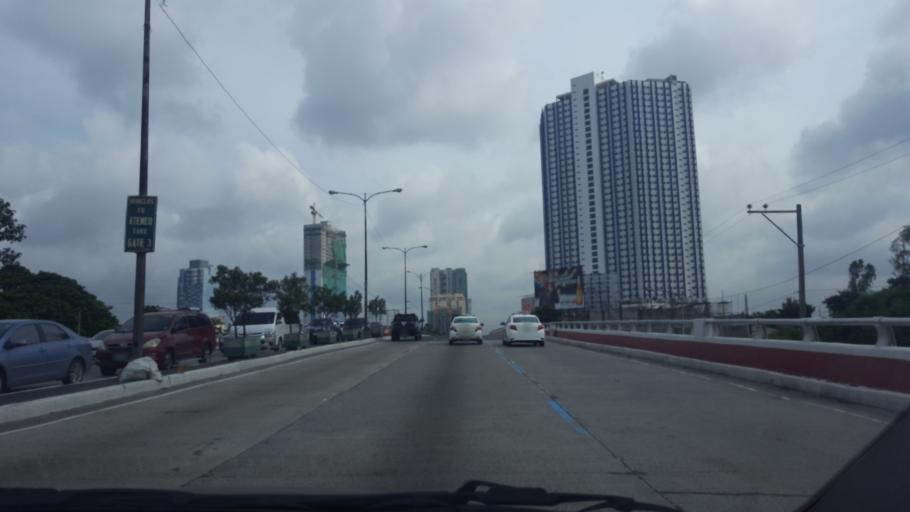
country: PH
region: Metro Manila
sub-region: Marikina
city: Calumpang
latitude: 14.6296
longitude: 121.0742
